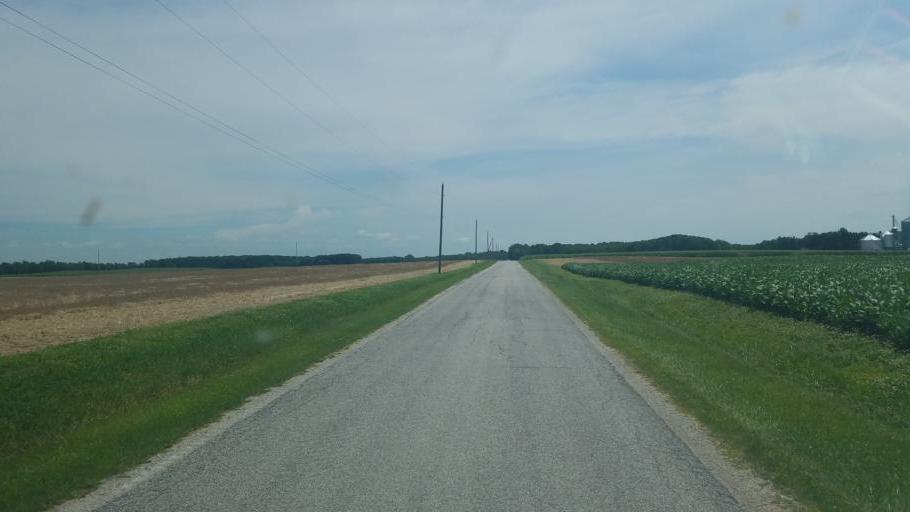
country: US
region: Ohio
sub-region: Crawford County
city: Bucyrus
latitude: 40.8708
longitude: -82.9010
